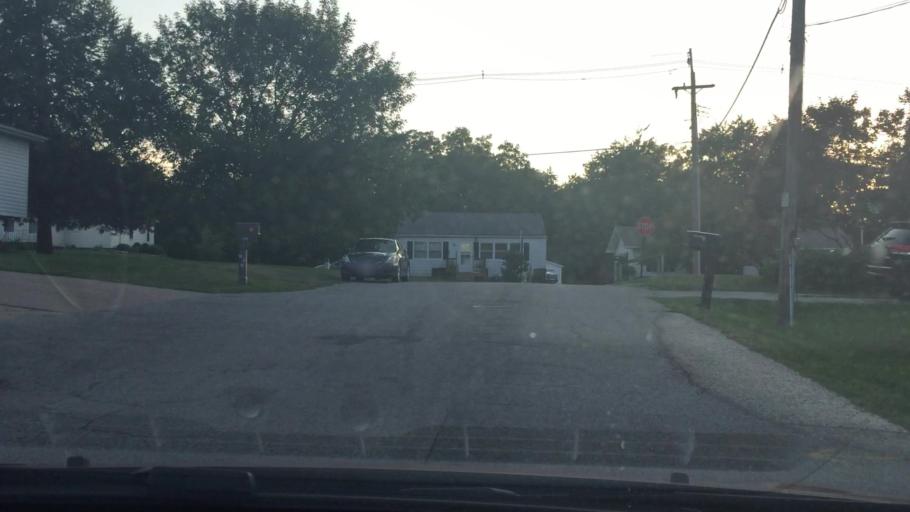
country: US
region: Iowa
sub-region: Muscatine County
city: Muscatine
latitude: 41.4320
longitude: -91.0643
